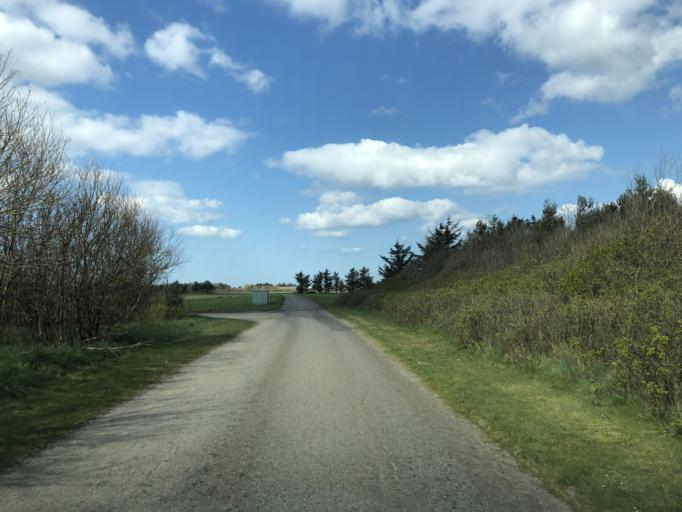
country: DK
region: Central Jutland
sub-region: Holstebro Kommune
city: Ulfborg
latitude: 56.3929
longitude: 8.1905
